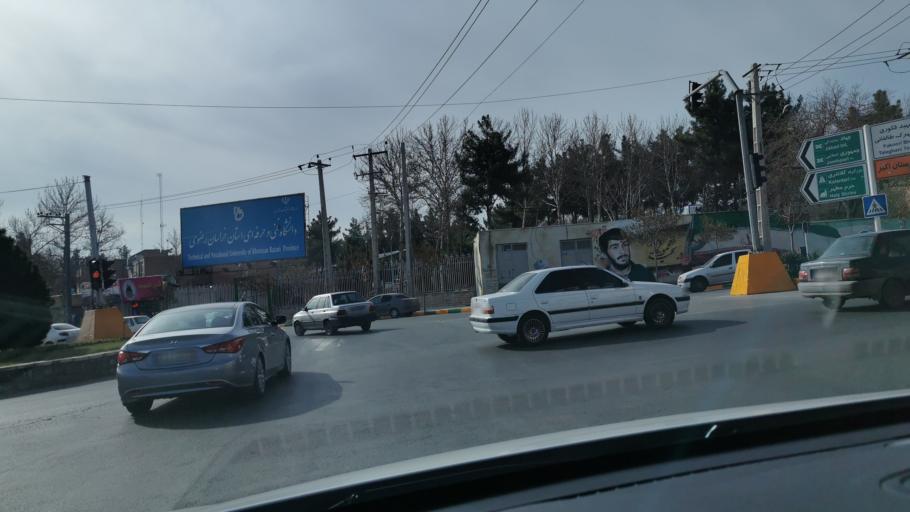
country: IR
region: Razavi Khorasan
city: Mashhad
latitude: 36.2844
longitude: 59.5485
